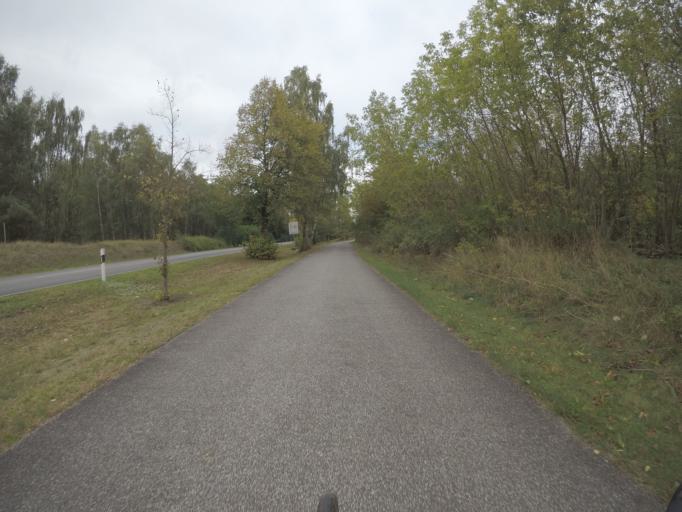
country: DE
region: Berlin
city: Buch
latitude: 52.6590
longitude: 13.4903
